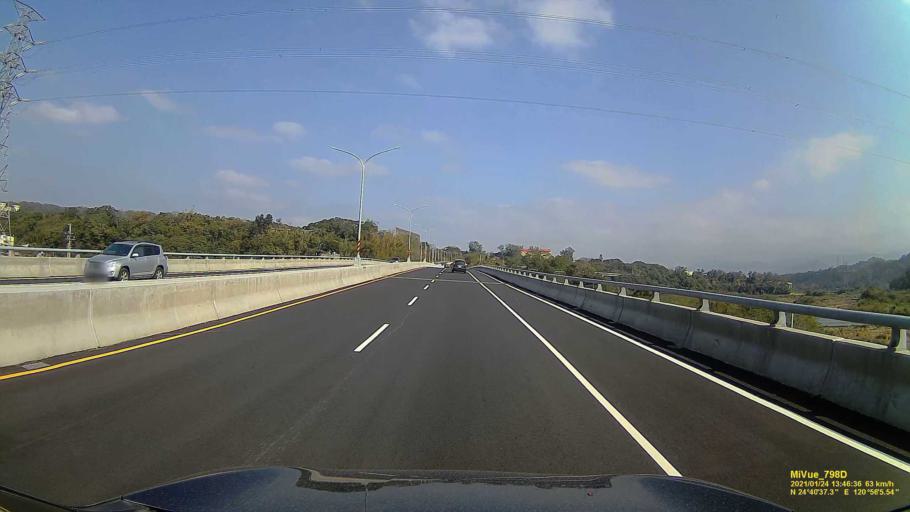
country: TW
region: Taiwan
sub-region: Hsinchu
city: Hsinchu
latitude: 24.6771
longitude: 120.9350
